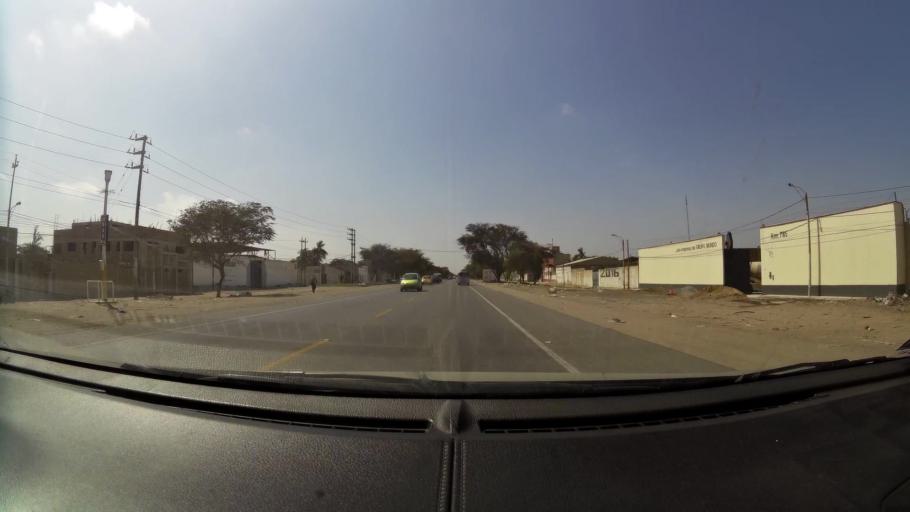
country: PE
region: Lambayeque
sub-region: Provincia de Chiclayo
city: Reque
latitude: -6.8297
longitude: -79.8294
